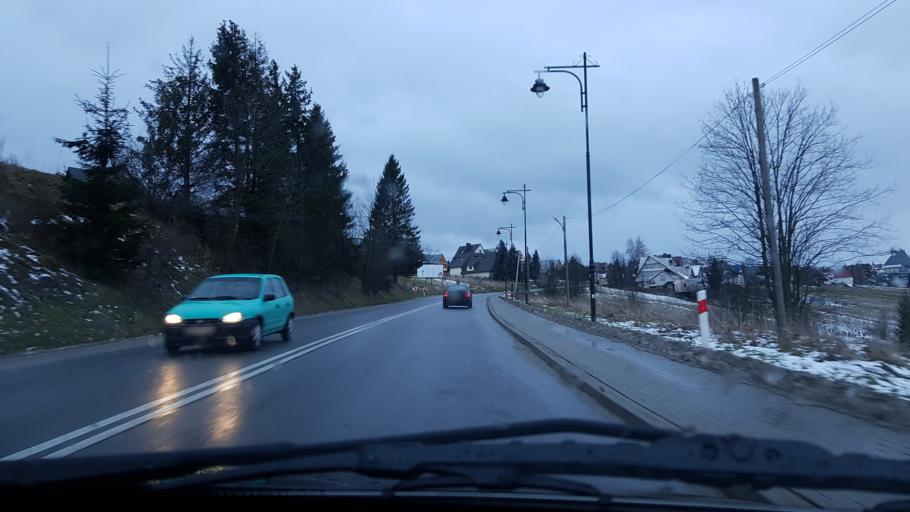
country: PL
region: Lesser Poland Voivodeship
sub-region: Powiat tatrzanski
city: Bukowina Tatrzanska
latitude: 49.3487
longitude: 20.1168
